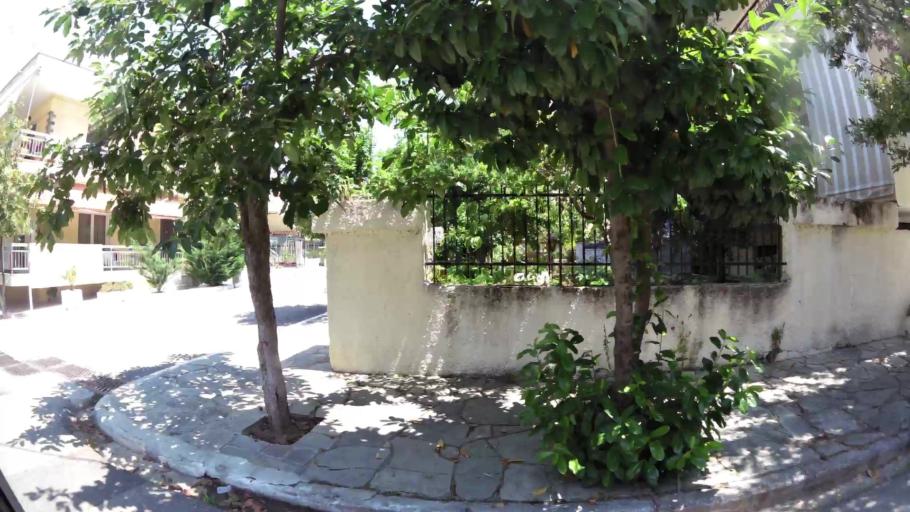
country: GR
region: Central Macedonia
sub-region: Nomos Thessalonikis
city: Nea Michaniona
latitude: 40.4754
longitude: 22.8701
